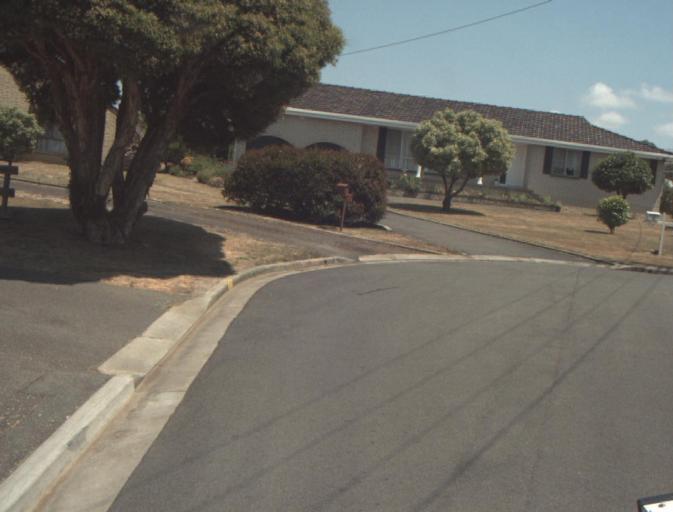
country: AU
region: Tasmania
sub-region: Launceston
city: Newstead
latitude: -41.4696
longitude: 147.1799
